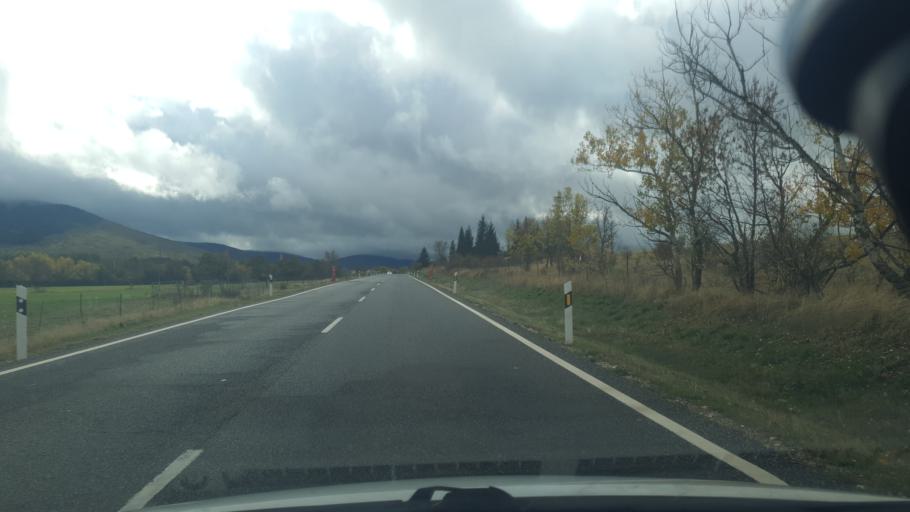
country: ES
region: Castille and Leon
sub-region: Provincia de Segovia
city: Collado Hermoso
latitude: 41.0456
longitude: -3.9132
